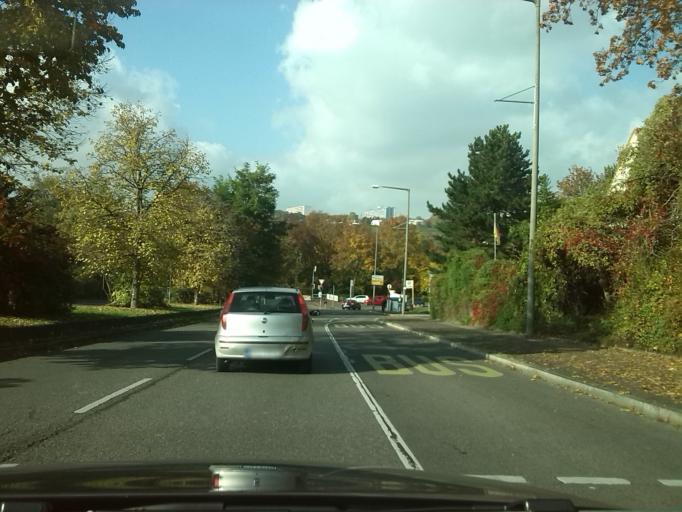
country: DE
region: Baden-Wuerttemberg
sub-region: Regierungsbezirk Stuttgart
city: Stuttgart Muehlhausen
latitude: 48.8324
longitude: 9.2181
